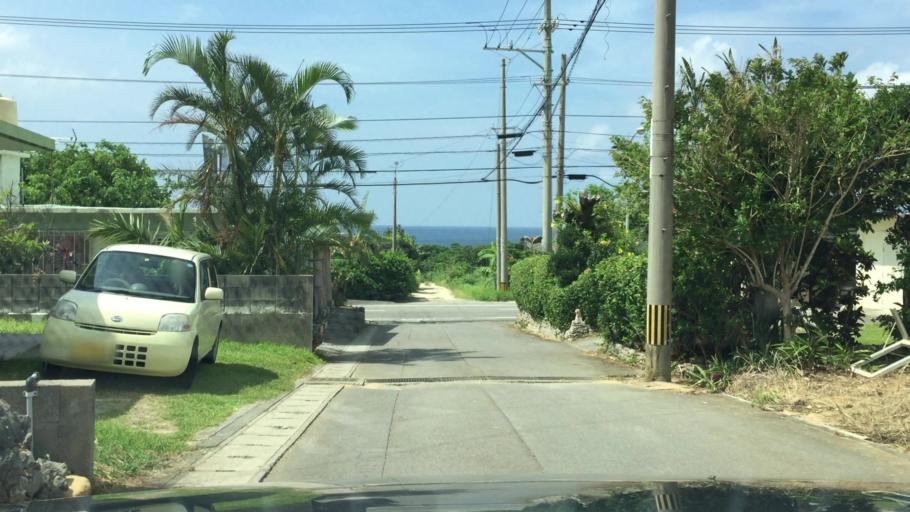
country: JP
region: Okinawa
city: Ishigaki
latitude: 24.4537
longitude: 124.1950
